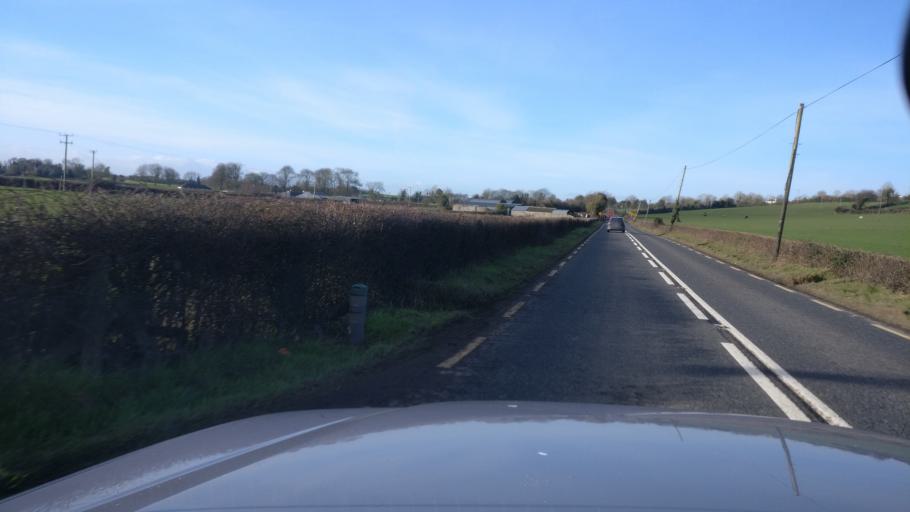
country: IE
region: Leinster
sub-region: Uibh Fhaili
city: Tullamore
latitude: 53.1944
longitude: -7.4142
